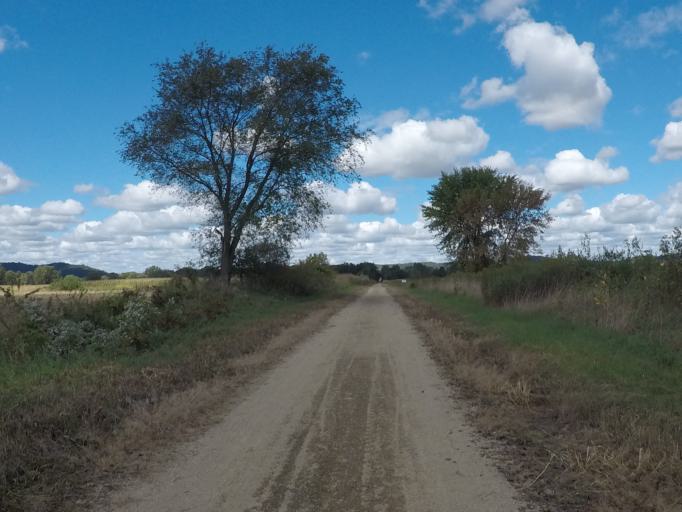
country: US
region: Wisconsin
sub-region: Richland County
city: Richland Center
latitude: 43.2962
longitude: -90.3311
